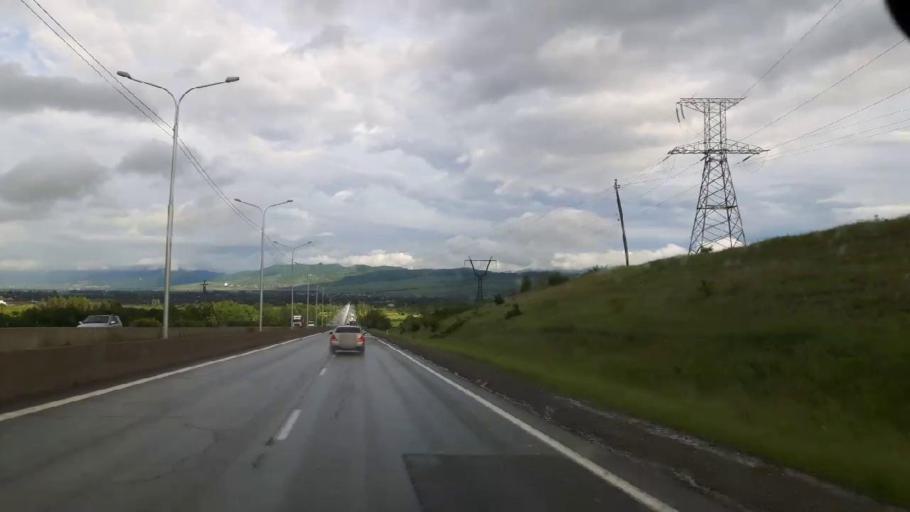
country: GE
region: Shida Kartli
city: Kaspi
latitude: 41.9281
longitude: 44.5317
